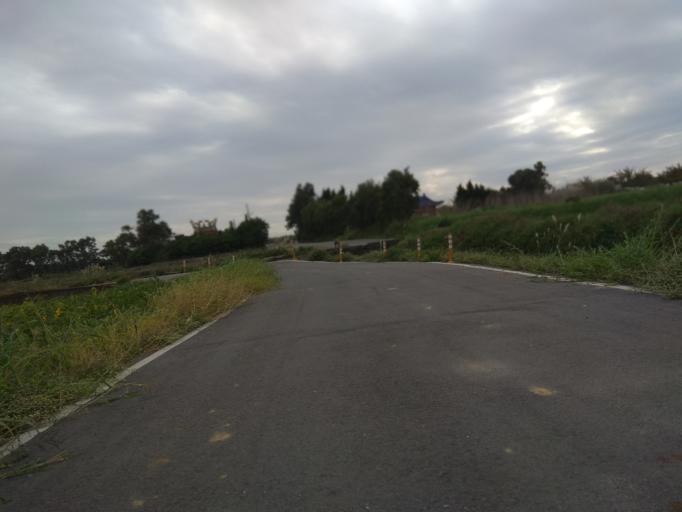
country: TW
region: Taiwan
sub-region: Hsinchu
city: Zhubei
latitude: 24.9770
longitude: 121.0299
